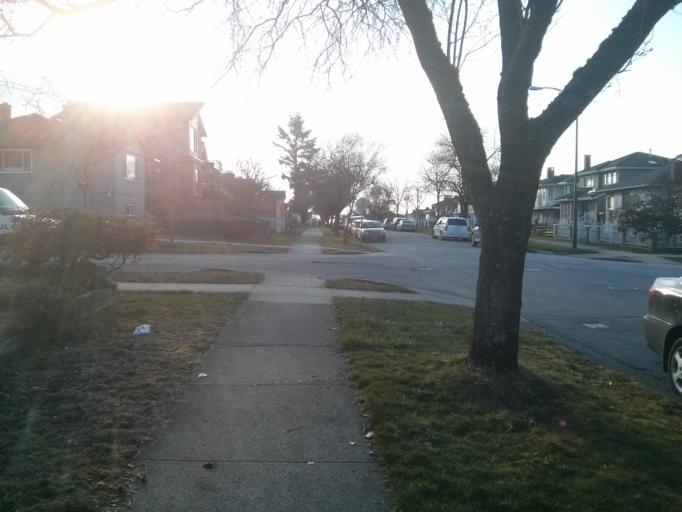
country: CA
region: British Columbia
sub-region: Fraser Valley Regional District
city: North Vancouver
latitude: 49.2478
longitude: -123.0307
